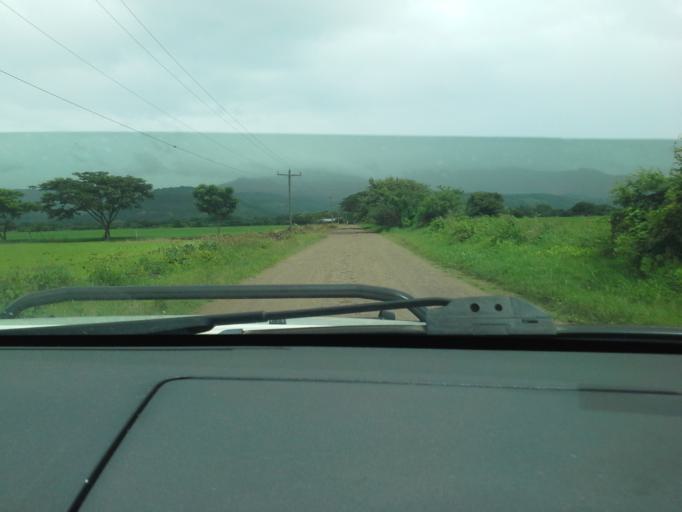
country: NI
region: Matagalpa
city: Ciudad Dario
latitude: 12.8597
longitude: -86.1851
